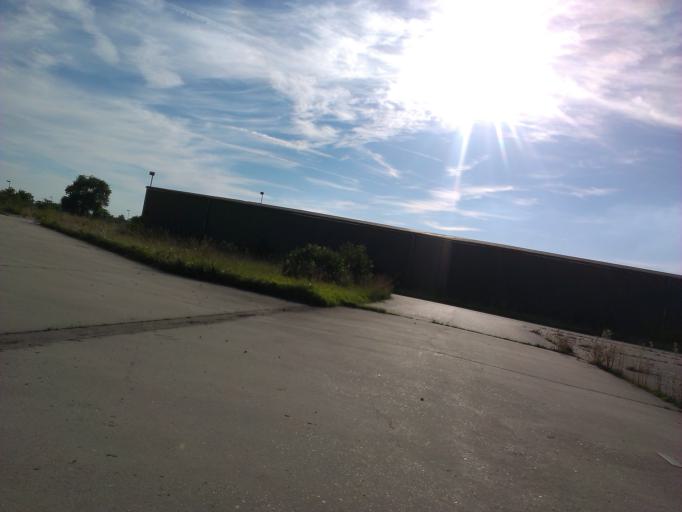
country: DE
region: Baden-Wuerttemberg
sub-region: Karlsruhe Region
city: Mannheim
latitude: 49.5003
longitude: 8.5178
